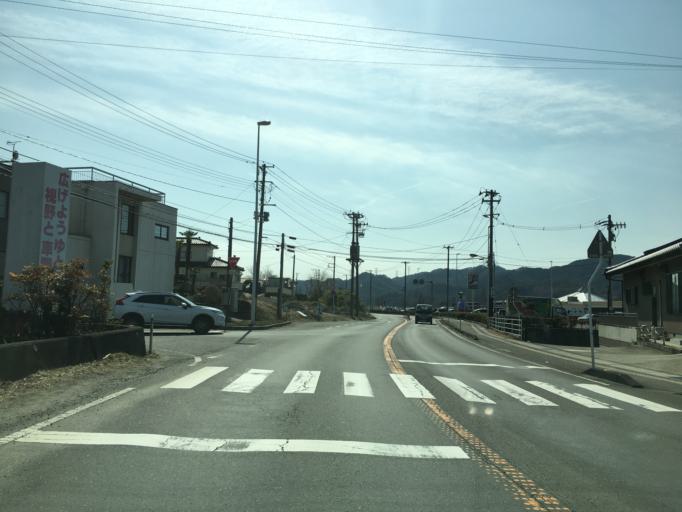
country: JP
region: Ibaraki
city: Daigo
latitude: 36.9513
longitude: 140.4155
